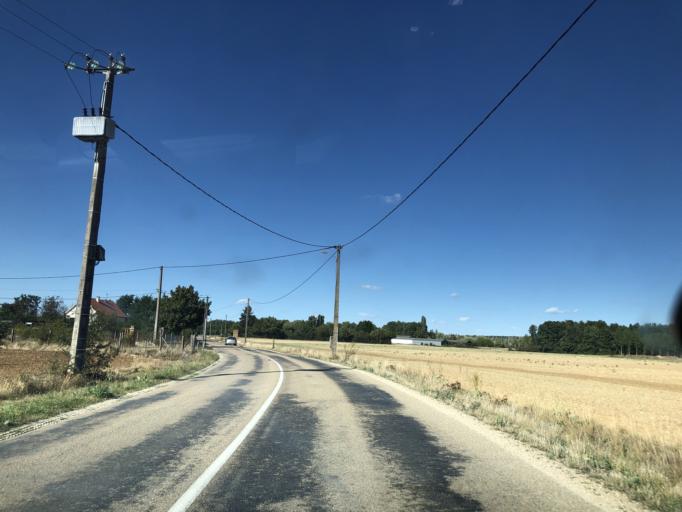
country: FR
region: Bourgogne
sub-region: Departement de l'Yonne
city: Appoigny
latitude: 47.8802
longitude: 3.5406
